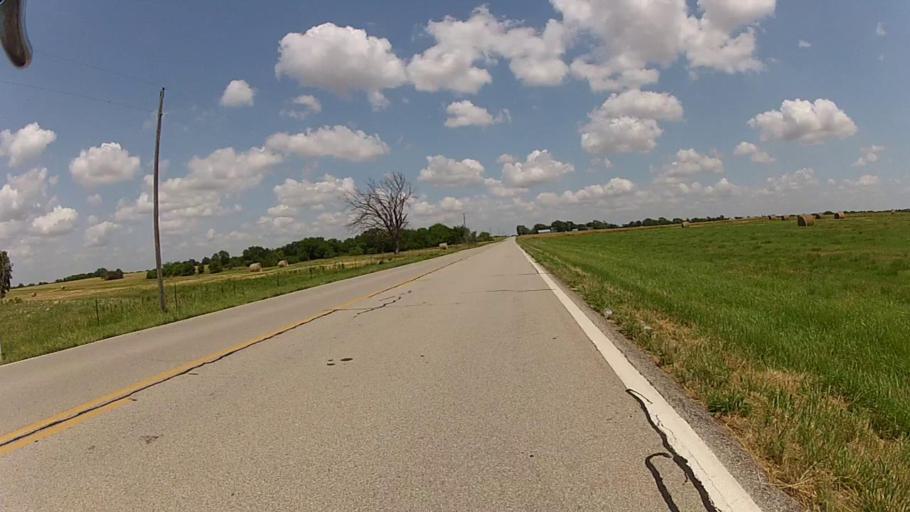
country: US
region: Kansas
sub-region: Labette County
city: Altamont
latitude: 37.1925
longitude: -95.3508
